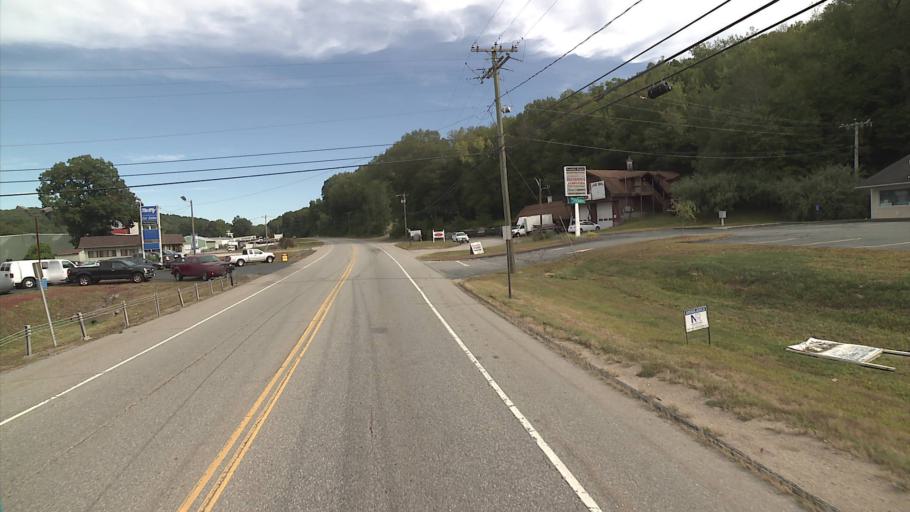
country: US
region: Connecticut
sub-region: New London County
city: Baltic
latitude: 41.5760
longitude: -72.1316
